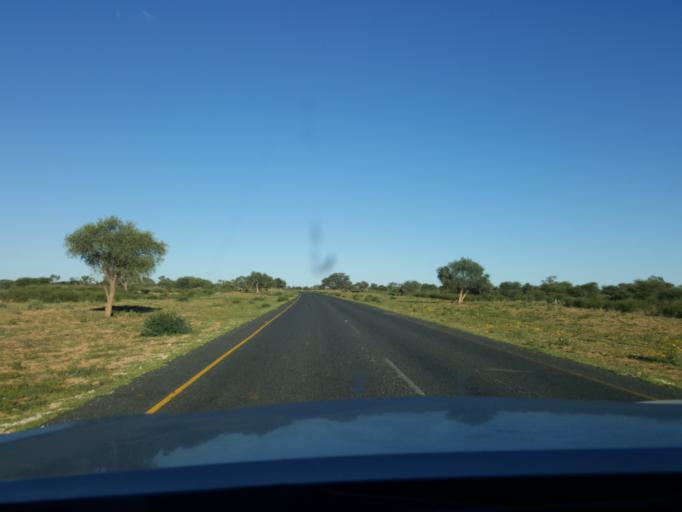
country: BW
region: Southern
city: Khakhea
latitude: -24.2514
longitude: 23.2940
